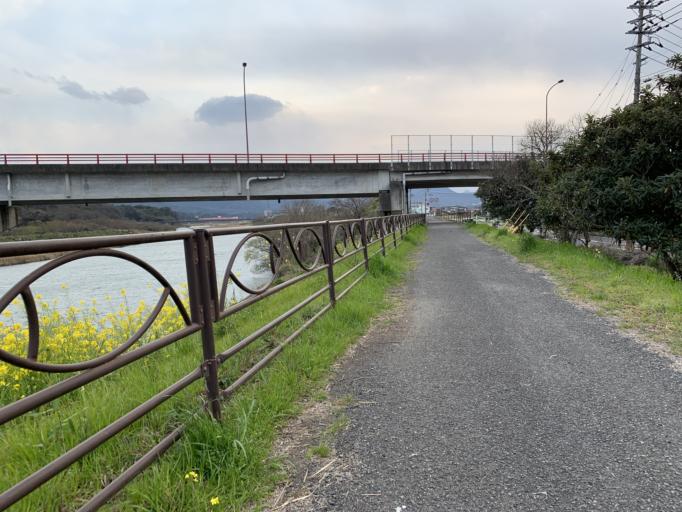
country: JP
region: Oita
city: Bungo-Takada-shi
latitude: 33.5422
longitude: 131.3549
